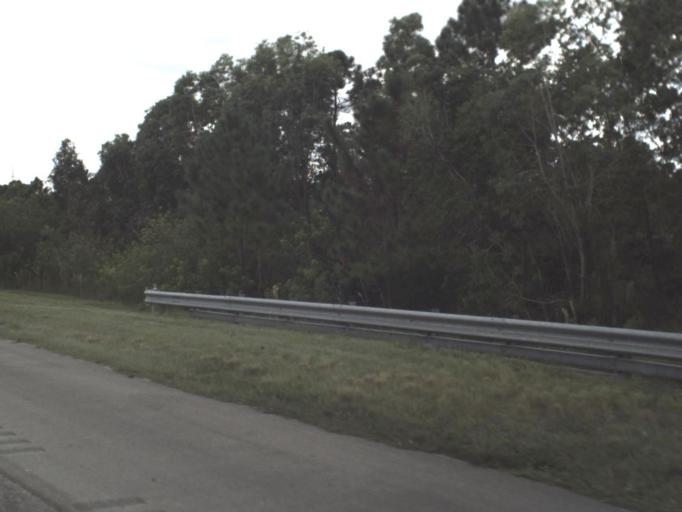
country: US
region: Florida
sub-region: Saint Lucie County
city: White City
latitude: 27.3525
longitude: -80.3745
